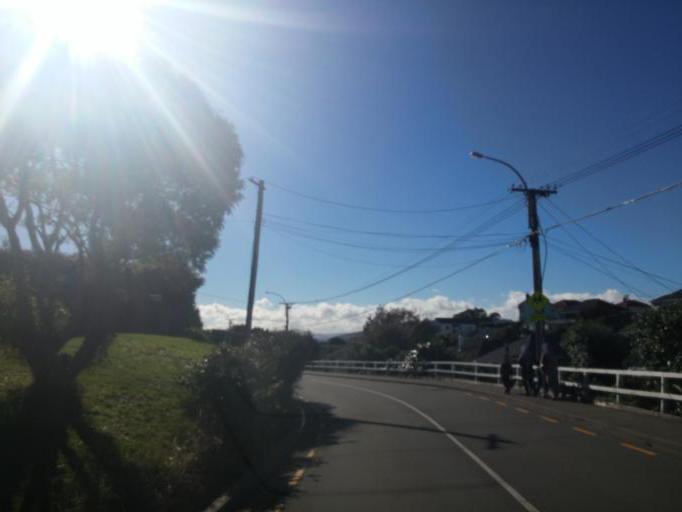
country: NZ
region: Wellington
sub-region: Wellington City
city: Wellington
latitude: -41.2276
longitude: 174.7992
